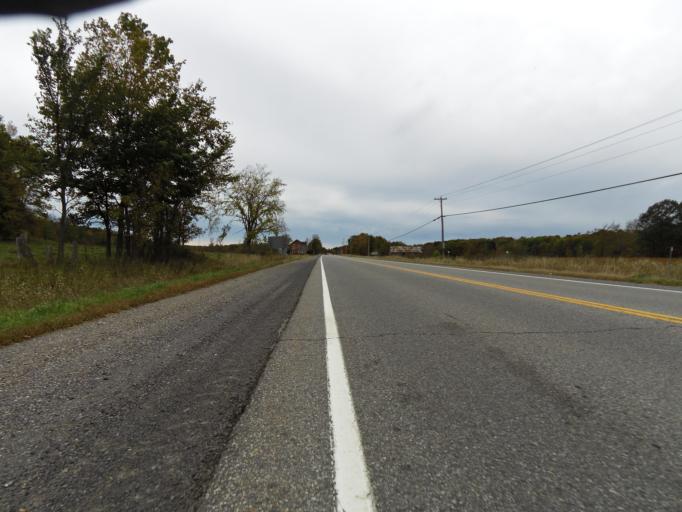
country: CA
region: Ontario
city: Gananoque
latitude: 44.4259
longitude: -76.2975
